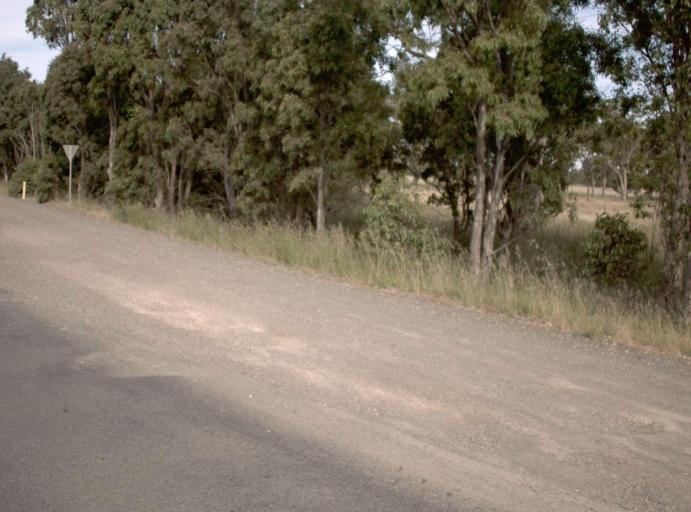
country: AU
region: Victoria
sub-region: Wellington
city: Heyfield
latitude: -38.0584
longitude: 146.6614
